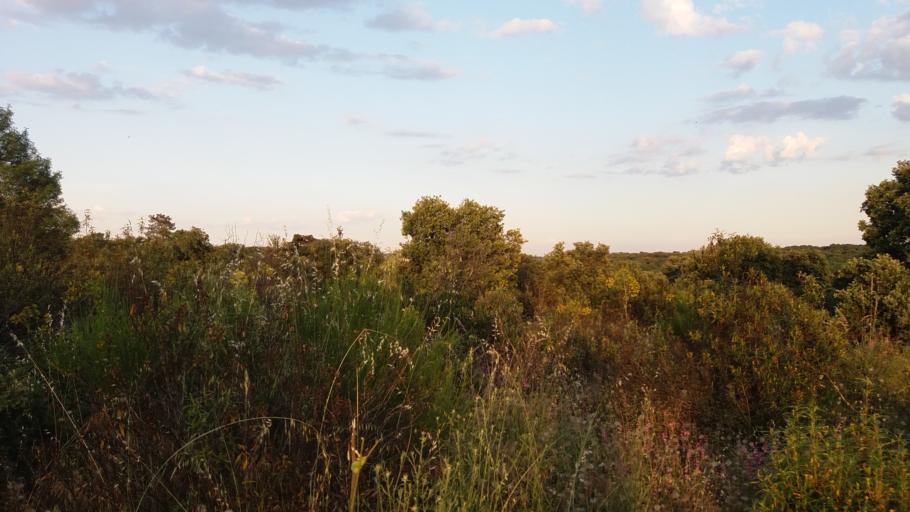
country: ES
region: Madrid
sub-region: Provincia de Madrid
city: Galapagar
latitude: 40.5805
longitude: -3.9872
